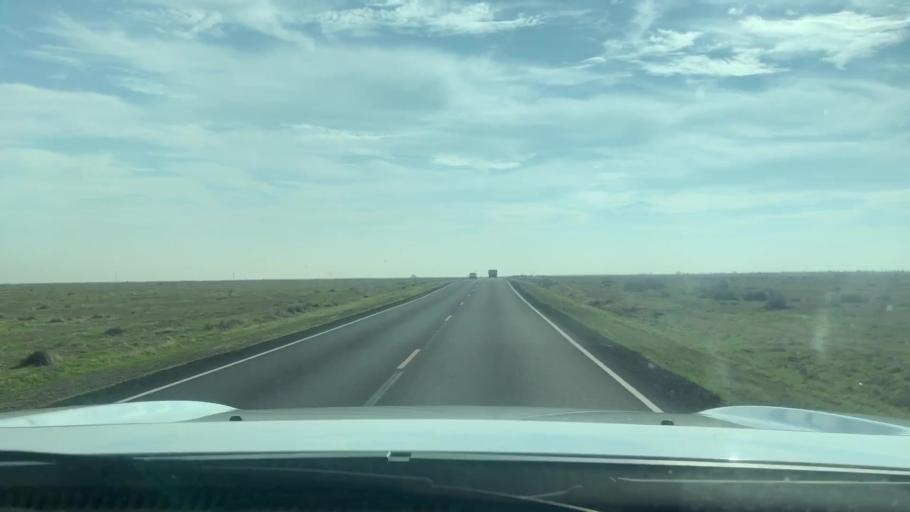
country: US
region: California
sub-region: Kern County
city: Lost Hills
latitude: 35.5710
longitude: -119.8137
